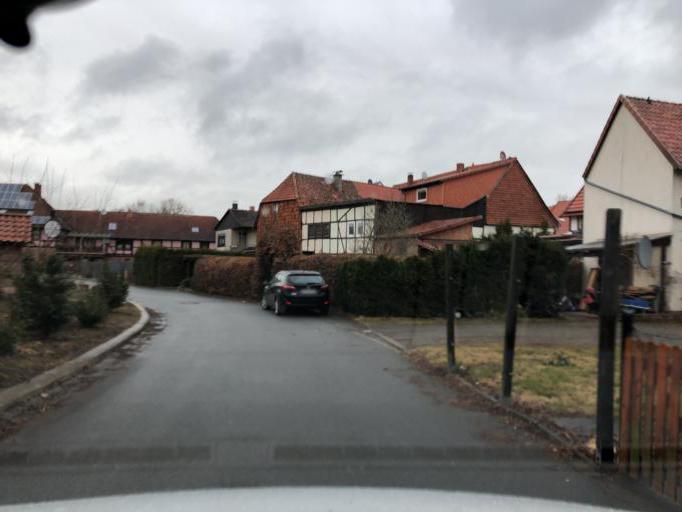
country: DE
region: Lower Saxony
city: Gieboldehausen
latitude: 51.6125
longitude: 10.2171
